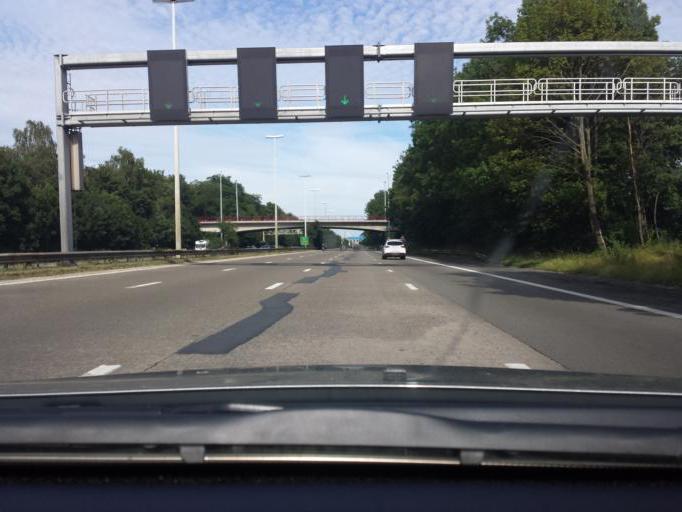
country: BE
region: Flanders
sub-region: Provincie Vlaams-Brabant
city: Kraainem
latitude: 50.8693
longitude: 4.4851
